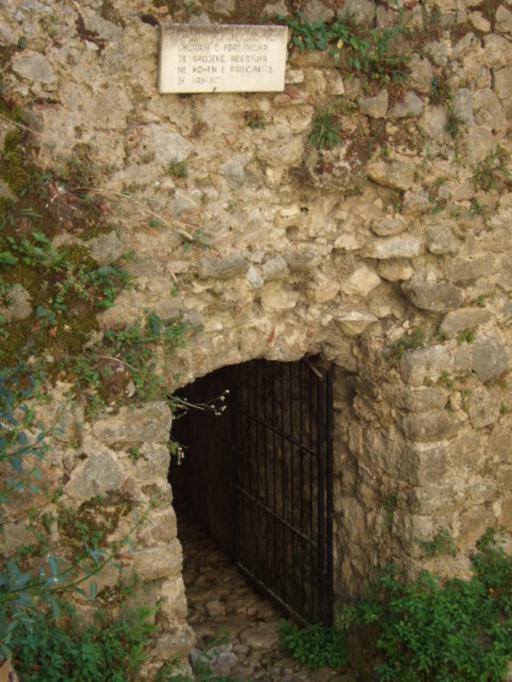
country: AL
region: Durres
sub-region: Rrethi i Krujes
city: Kruje
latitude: 41.5061
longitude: 19.7928
